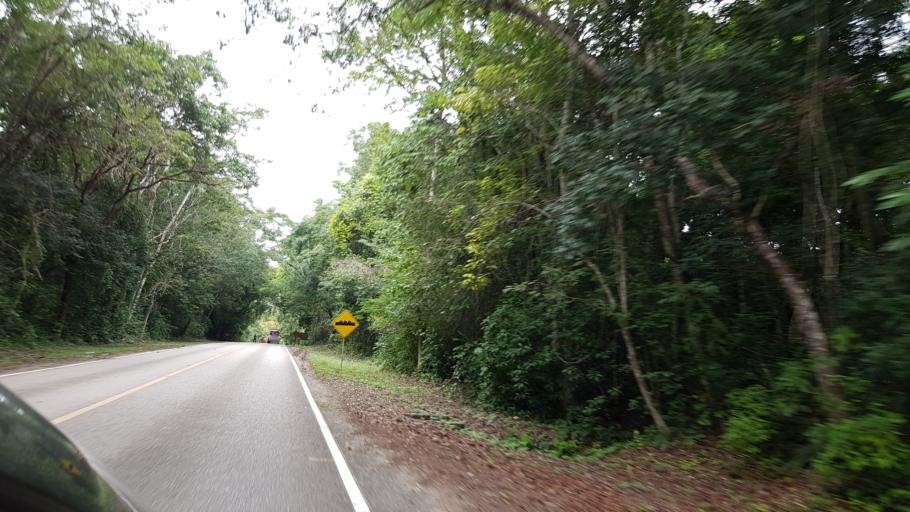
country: GT
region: Peten
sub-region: Municipio de San Jose
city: San Jose
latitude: 17.2215
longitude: -89.6117
